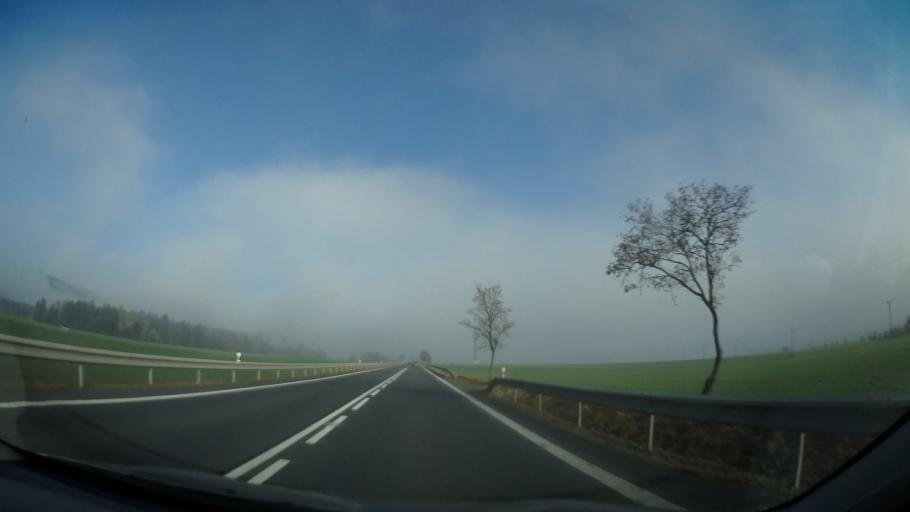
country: CZ
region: Vysocina
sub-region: Okres Zd'ar nad Sazavou
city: Nove Veseli
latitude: 49.4951
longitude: 15.9867
